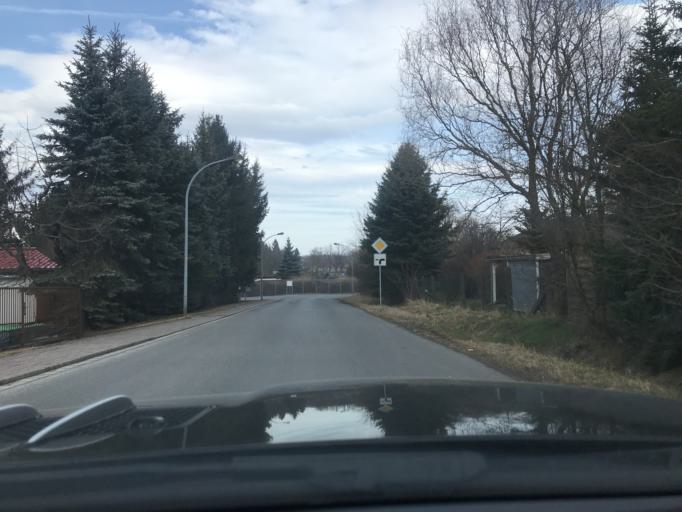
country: DE
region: Thuringia
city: Muehlhausen
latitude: 51.1996
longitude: 10.4319
